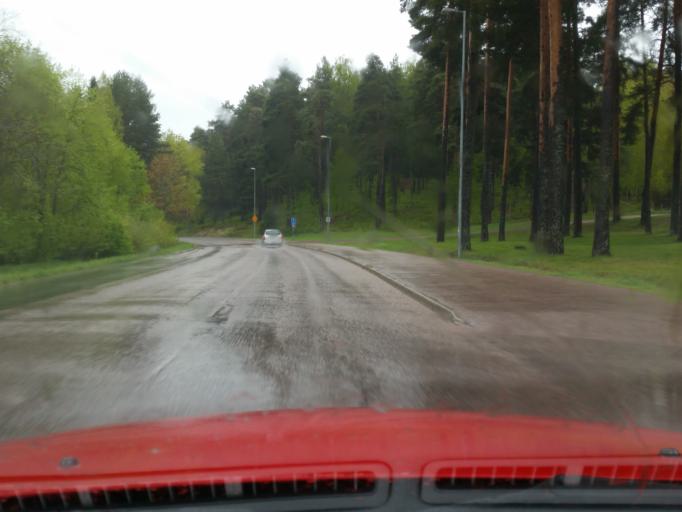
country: SE
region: Dalarna
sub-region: Hedemora Kommun
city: Hedemora
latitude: 60.2925
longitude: 15.9754
